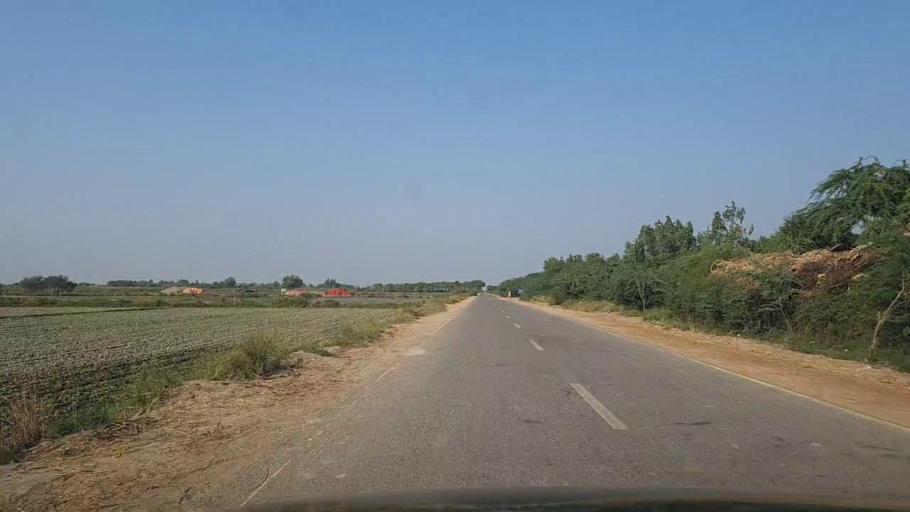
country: PK
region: Sindh
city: Thatta
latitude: 24.6176
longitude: 68.0515
